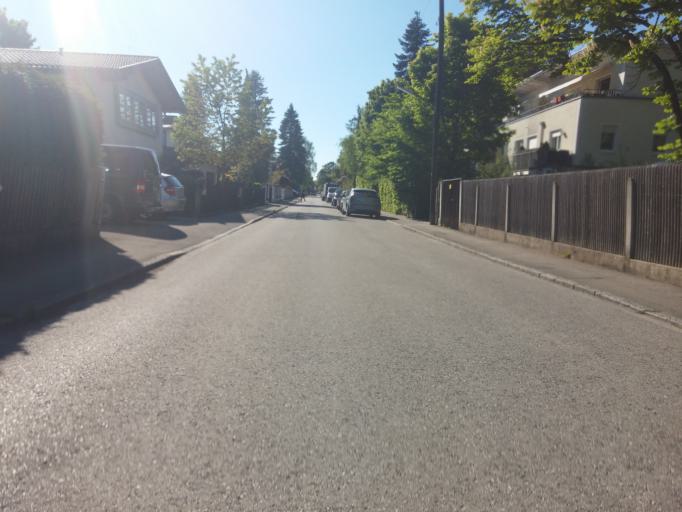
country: DE
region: Bavaria
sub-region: Upper Bavaria
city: Haar
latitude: 48.1156
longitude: 11.7073
